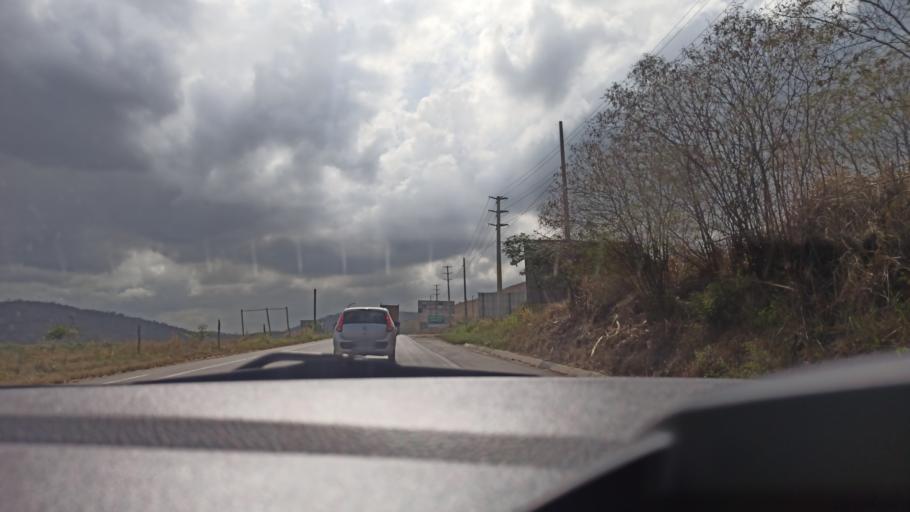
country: BR
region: Pernambuco
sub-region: Timbauba
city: Timbauba
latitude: -7.5212
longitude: -35.3047
